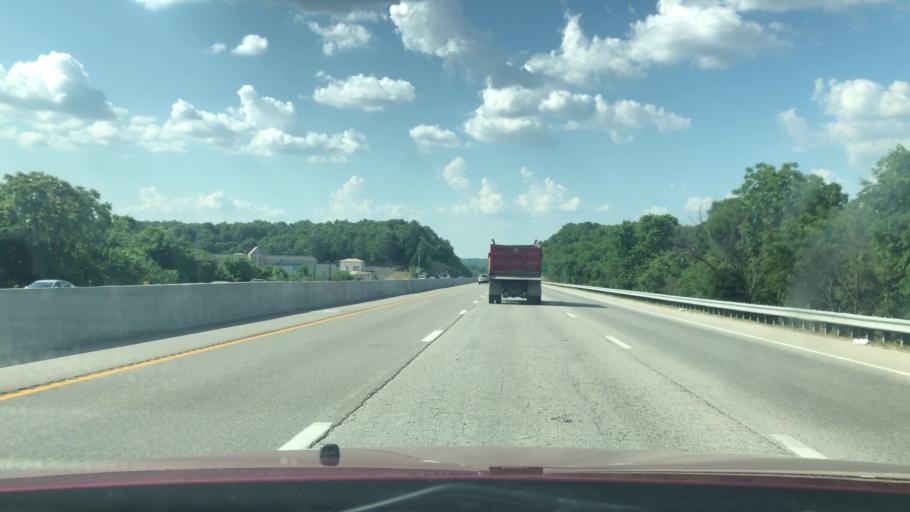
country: US
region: Missouri
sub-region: Christian County
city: Nixa
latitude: 37.1097
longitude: -93.2333
